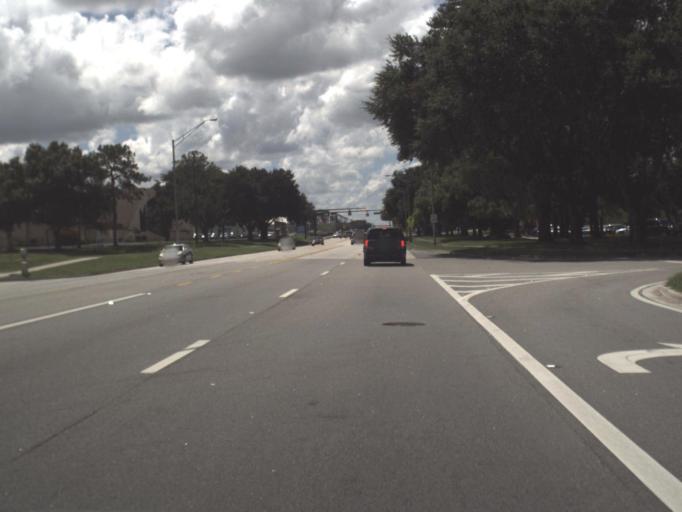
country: US
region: Florida
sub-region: Polk County
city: Lakeland
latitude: 28.0794
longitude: -81.9534
